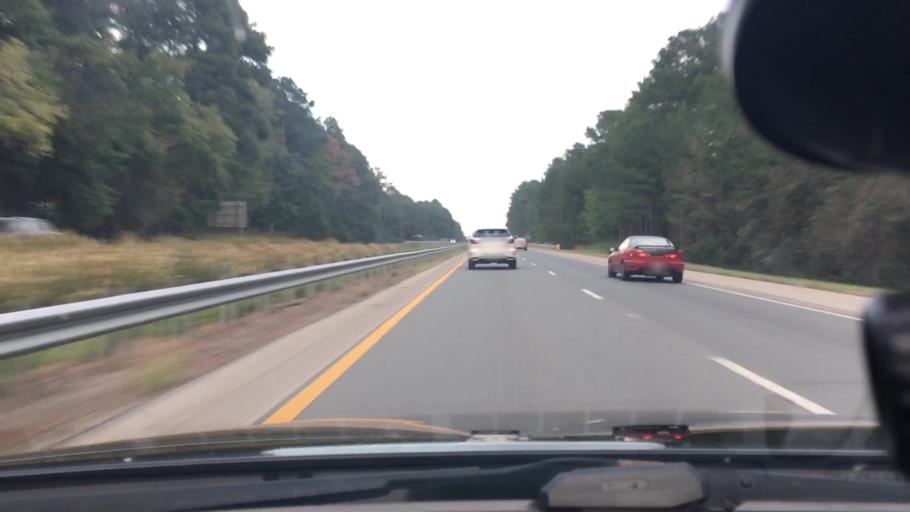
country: US
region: North Carolina
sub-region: Chatham County
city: Pittsboro
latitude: 35.6282
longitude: -79.0761
